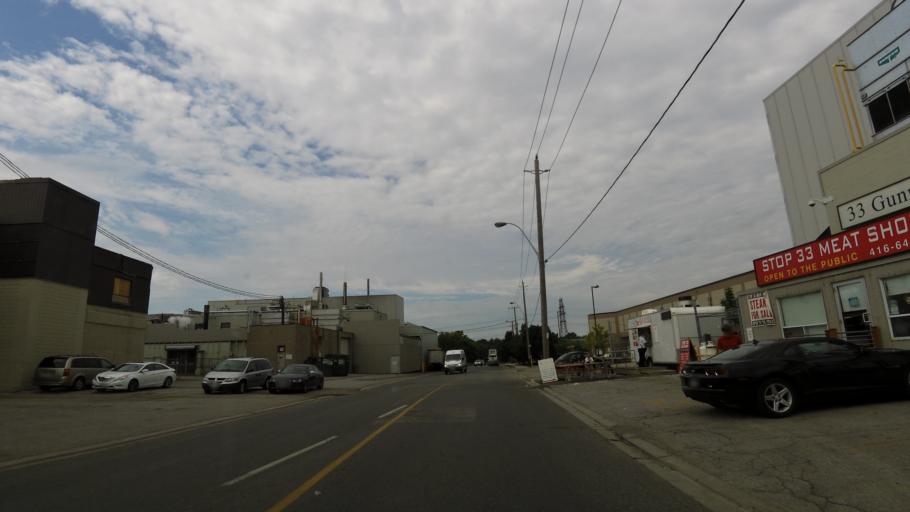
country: CA
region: Ontario
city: Toronto
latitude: 43.6736
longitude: -79.4724
